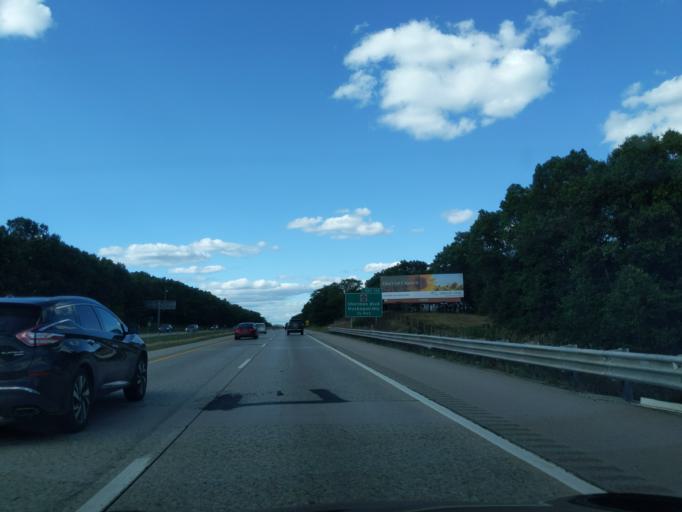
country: US
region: Michigan
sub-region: Muskegon County
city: Muskegon Heights
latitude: 43.1920
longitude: -86.2049
